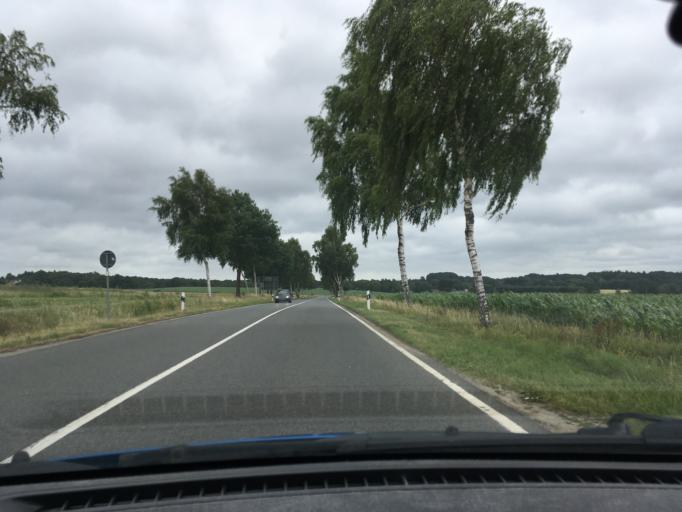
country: DE
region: Lower Saxony
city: Bispingen
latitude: 53.0986
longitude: 9.9800
